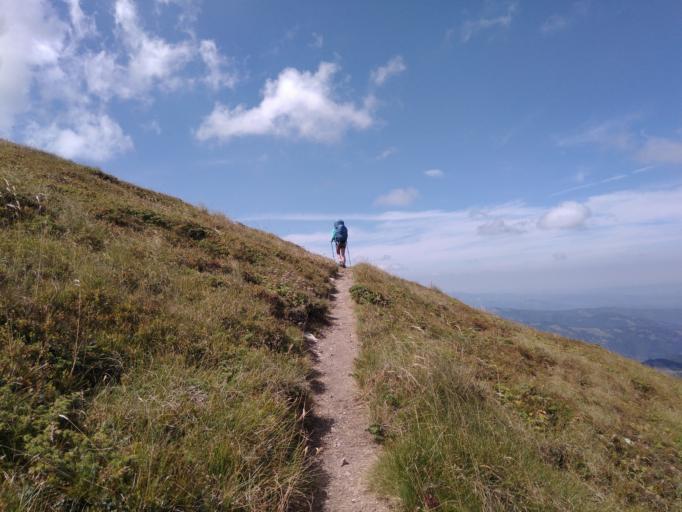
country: BG
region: Plovdiv
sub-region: Obshtina Karlovo
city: Karlovo
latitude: 42.7249
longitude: 24.7907
